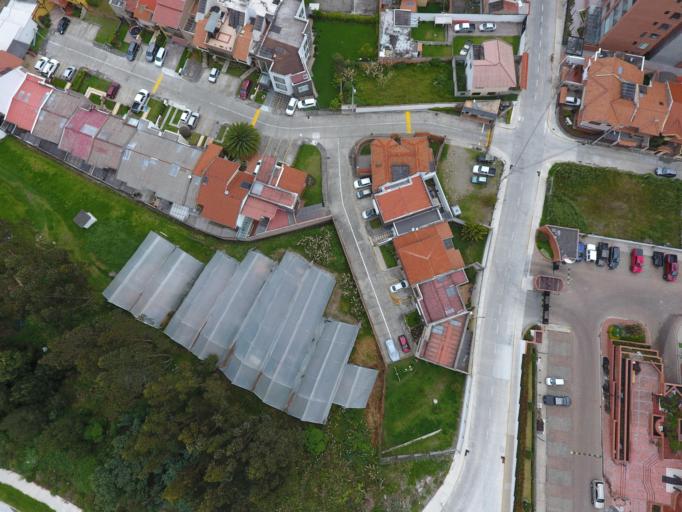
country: EC
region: Azuay
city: Cuenca
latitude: -2.9205
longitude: -79.0233
